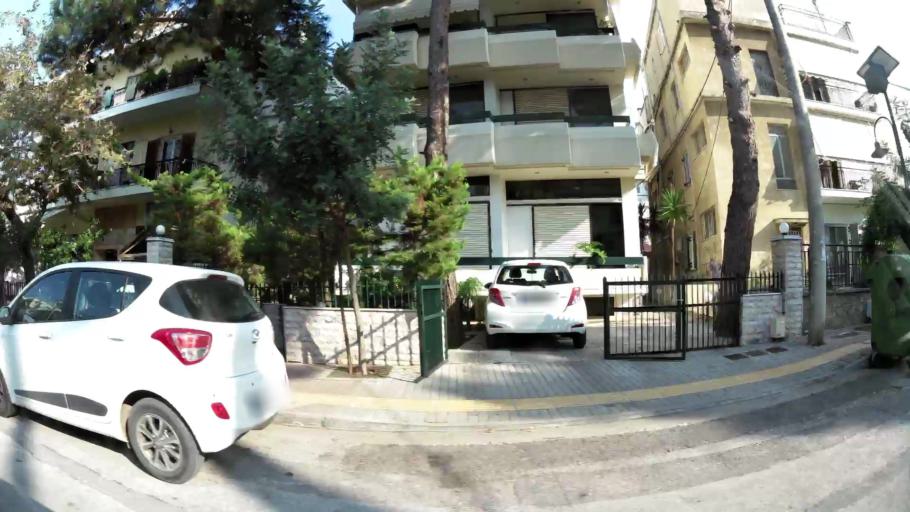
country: GR
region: Attica
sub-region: Nomarchia Athinas
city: Cholargos
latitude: 38.0007
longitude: 23.8113
